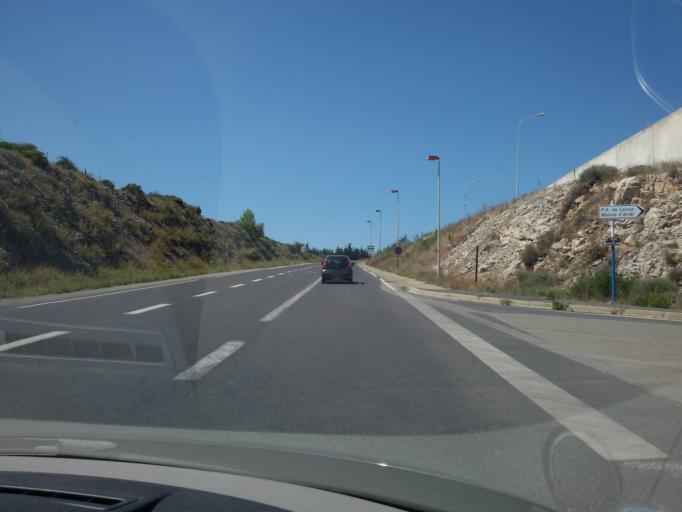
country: FR
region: Languedoc-Roussillon
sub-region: Departement de l'Herault
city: Saint-Jean-de-Vedas
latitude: 43.5449
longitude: 3.8289
